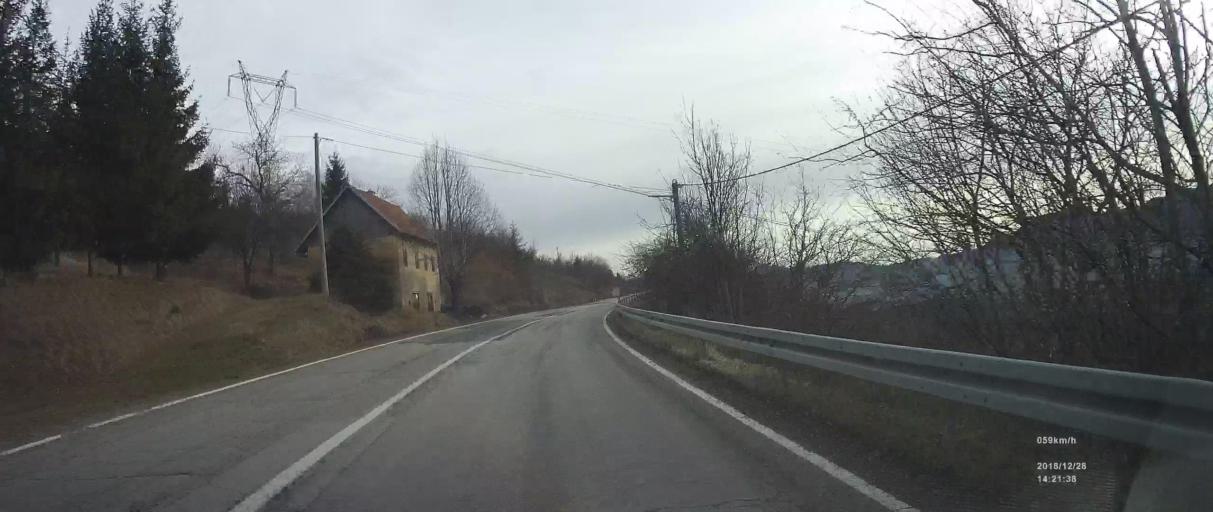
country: HR
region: Primorsko-Goranska
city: Vrbovsko
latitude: 45.3920
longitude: 15.0823
